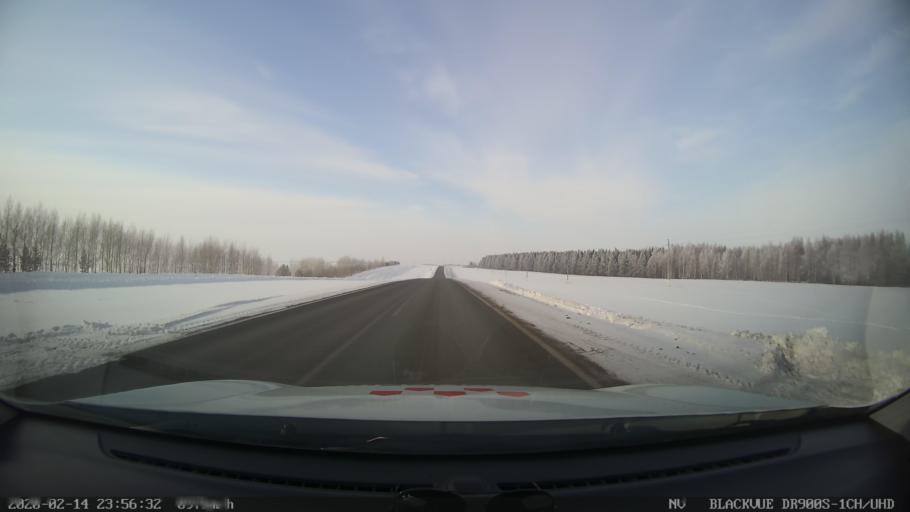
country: RU
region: Tatarstan
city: Kuybyshevskiy Zaton
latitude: 55.3257
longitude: 49.1282
